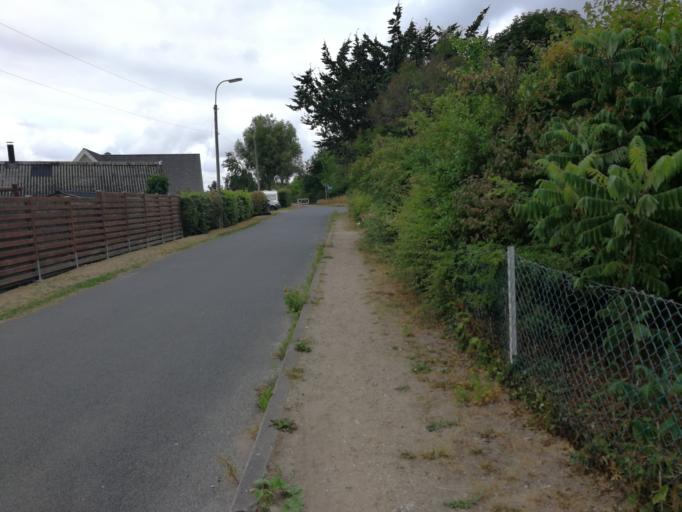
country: DK
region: Capital Region
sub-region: Hillerod Kommune
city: Hillerod
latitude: 55.9456
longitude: 12.2652
